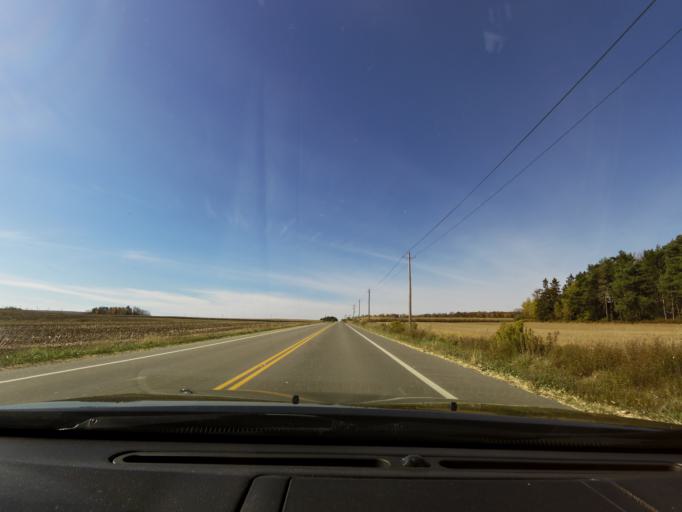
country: US
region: New York
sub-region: Wyoming County
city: Warsaw
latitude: 42.6526
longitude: -78.1717
